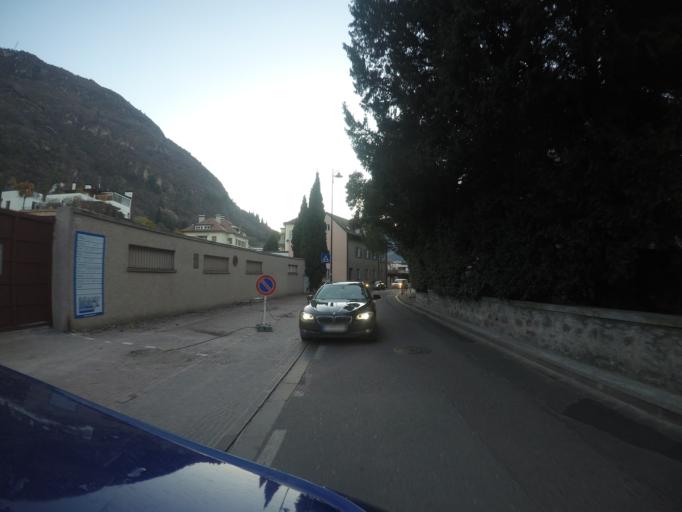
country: IT
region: Trentino-Alto Adige
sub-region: Bolzano
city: Bolzano
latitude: 46.5043
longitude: 11.3557
